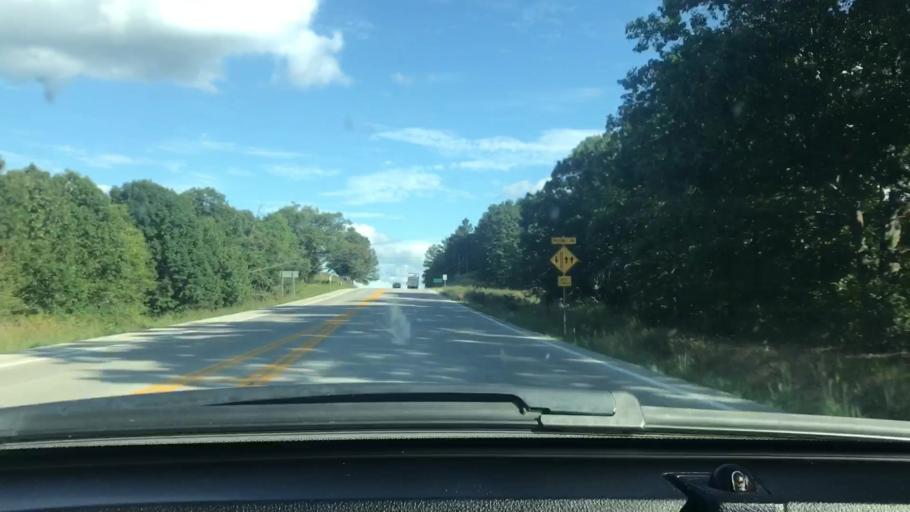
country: US
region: Missouri
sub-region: Howell County
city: West Plains
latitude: 36.6507
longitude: -91.6884
